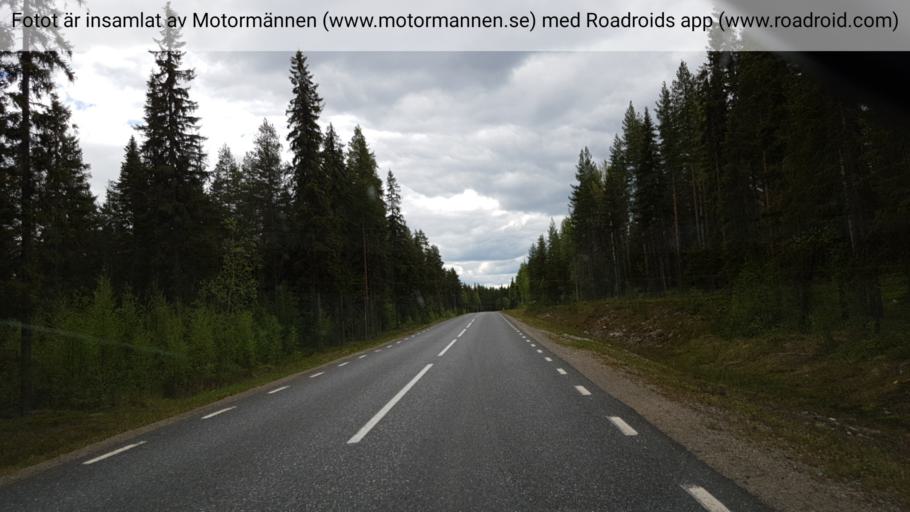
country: SE
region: Vaesterbotten
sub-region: Skelleftea Kommun
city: Langsele
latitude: 64.5666
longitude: 19.9289
